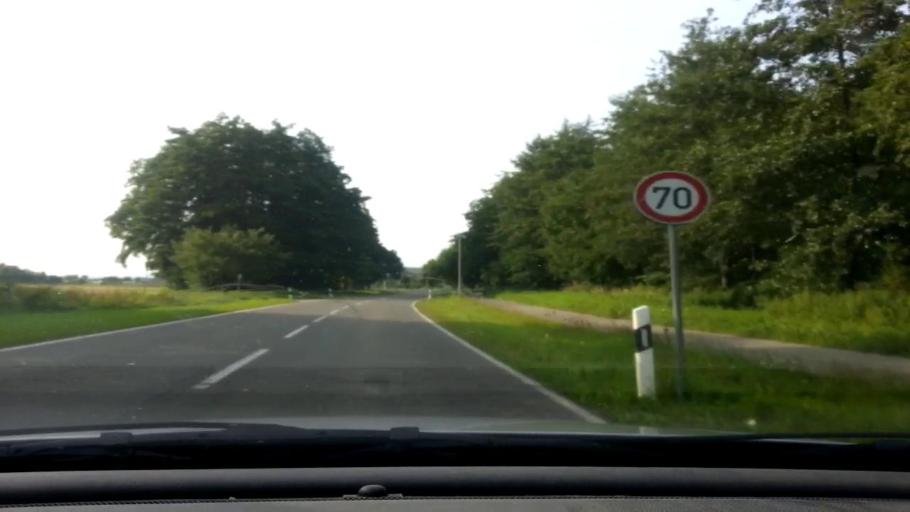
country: DE
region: Bavaria
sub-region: Upper Franconia
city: Memmelsdorf
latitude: 49.9250
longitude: 10.9582
